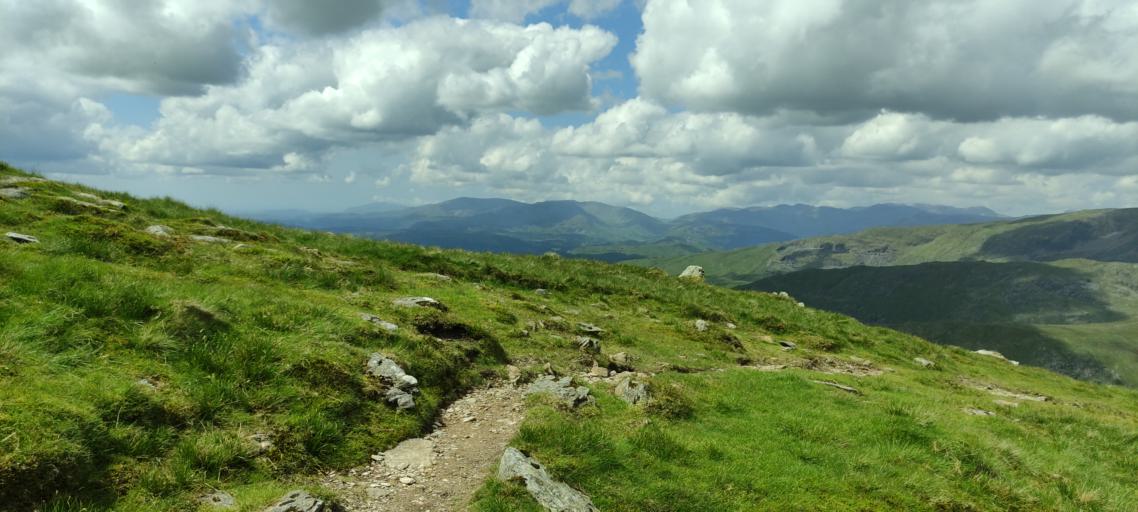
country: GB
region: England
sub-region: Cumbria
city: Windermere
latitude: 54.4625
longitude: -2.8717
